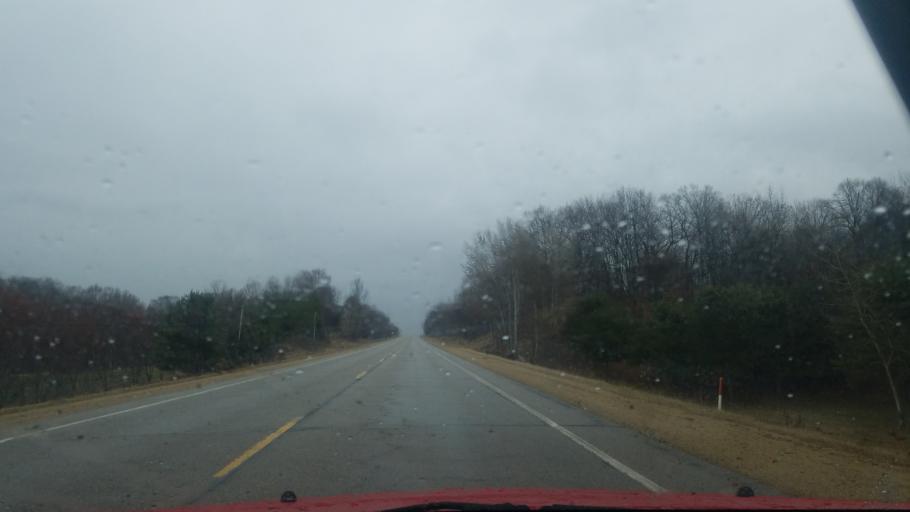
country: US
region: Wisconsin
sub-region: Dunn County
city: Menomonie
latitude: 44.9387
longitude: -91.9209
